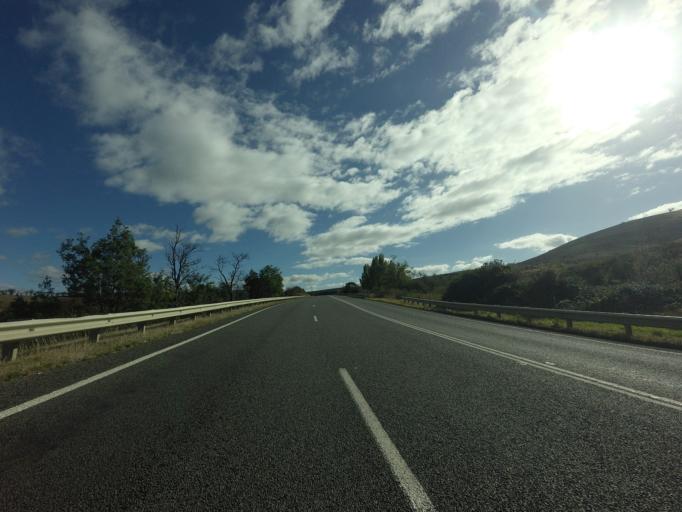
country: AU
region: Tasmania
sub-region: Derwent Valley
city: New Norfolk
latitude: -42.7203
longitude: 146.9482
